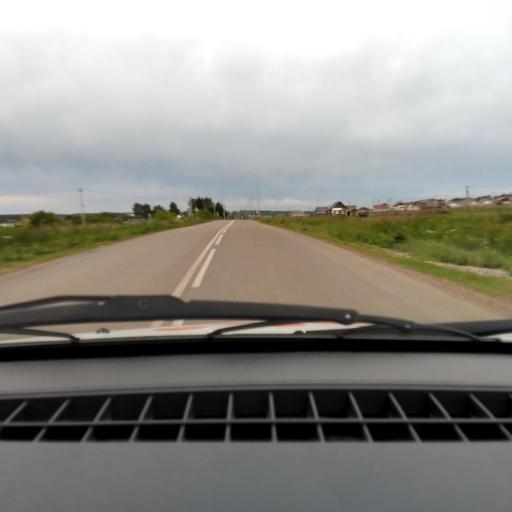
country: RU
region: Bashkortostan
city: Avdon
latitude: 54.5579
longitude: 55.7631
